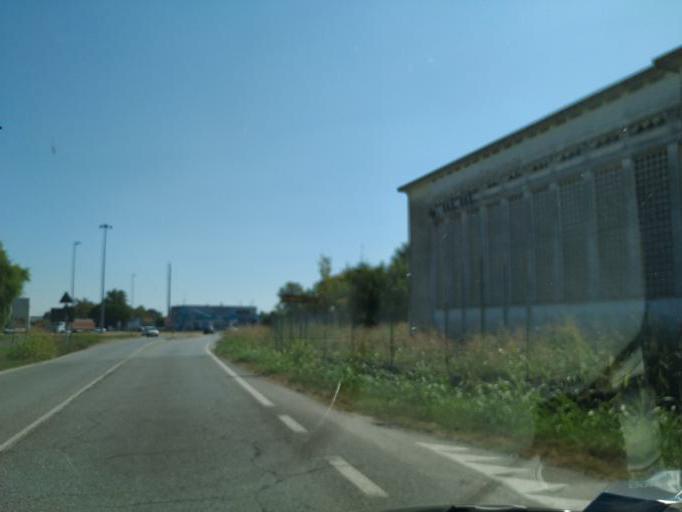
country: IT
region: Emilia-Romagna
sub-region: Provincia di Ferrara
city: Copparo
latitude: 44.8889
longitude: 11.8097
